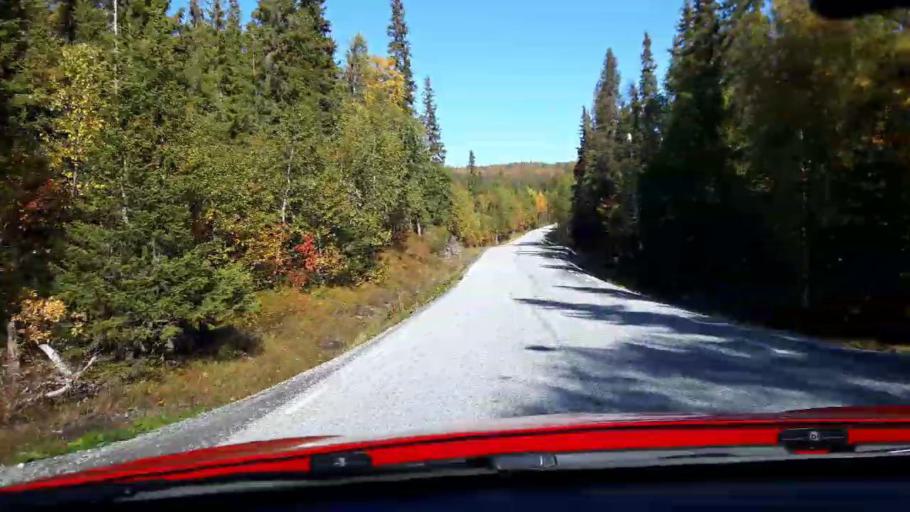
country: NO
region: Nord-Trondelag
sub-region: Royrvik
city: Royrvik
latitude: 64.8129
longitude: 14.1744
